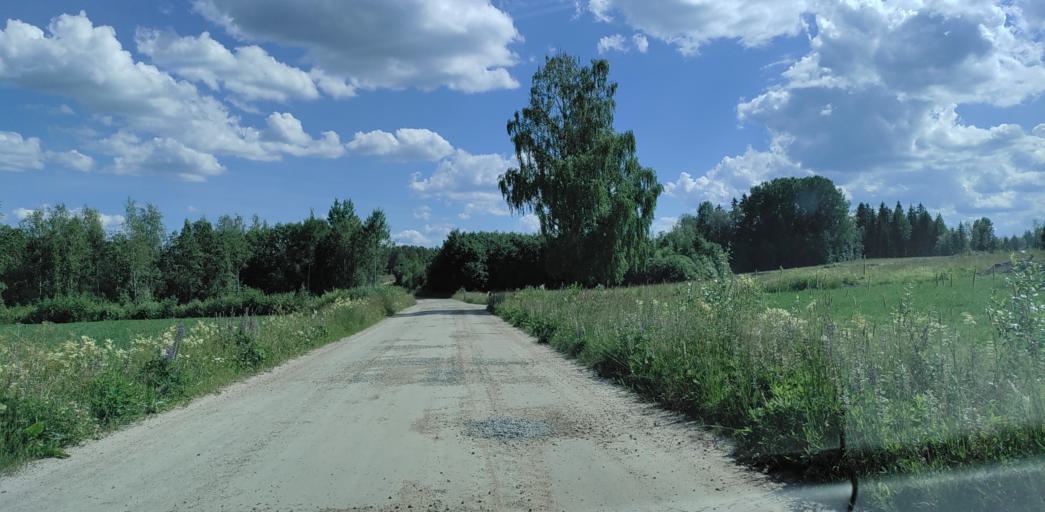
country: SE
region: Vaermland
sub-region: Hagfors Kommun
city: Ekshaerad
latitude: 60.1258
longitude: 13.4776
